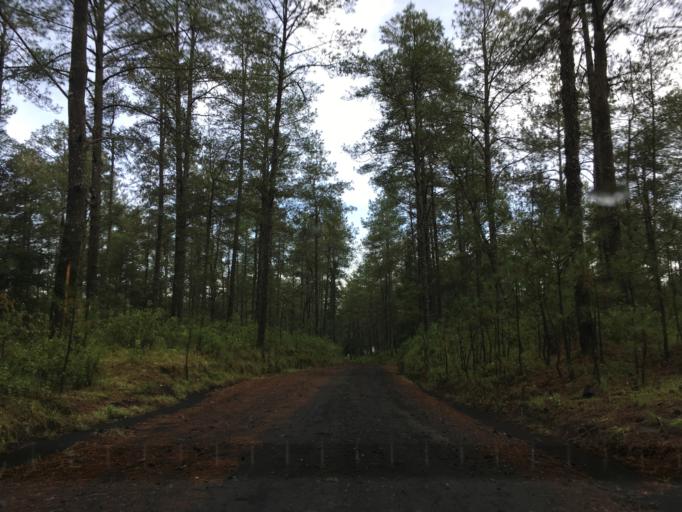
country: MX
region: Michoacan
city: Angahuan
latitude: 19.4990
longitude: -102.2069
